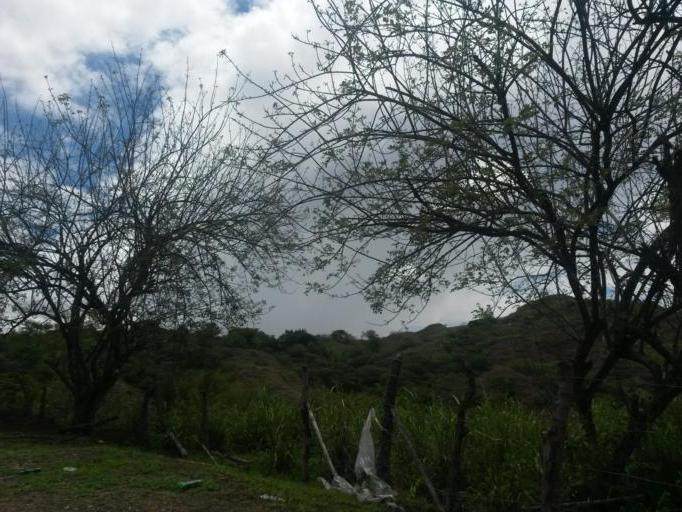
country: CO
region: Cauca
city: El Bordo
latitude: 2.0910
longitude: -76.9986
